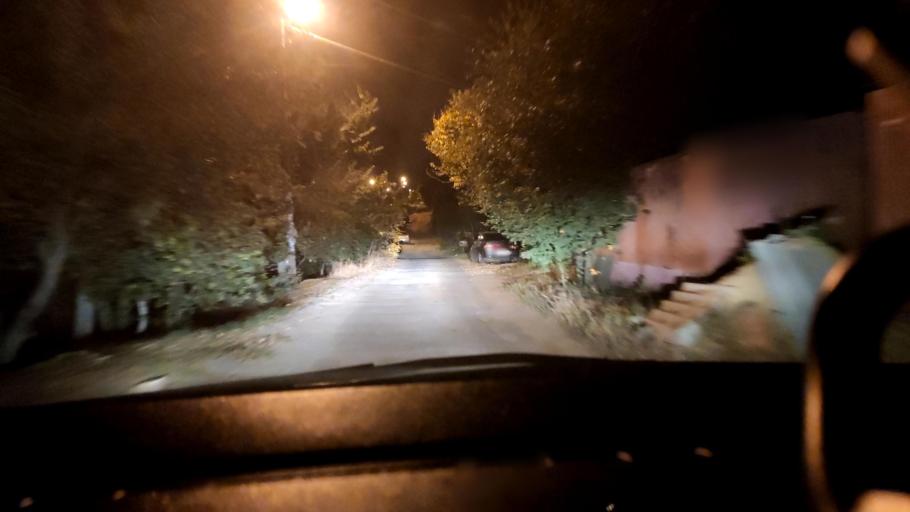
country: RU
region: Voronezj
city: Voronezh
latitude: 51.6385
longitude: 39.1898
